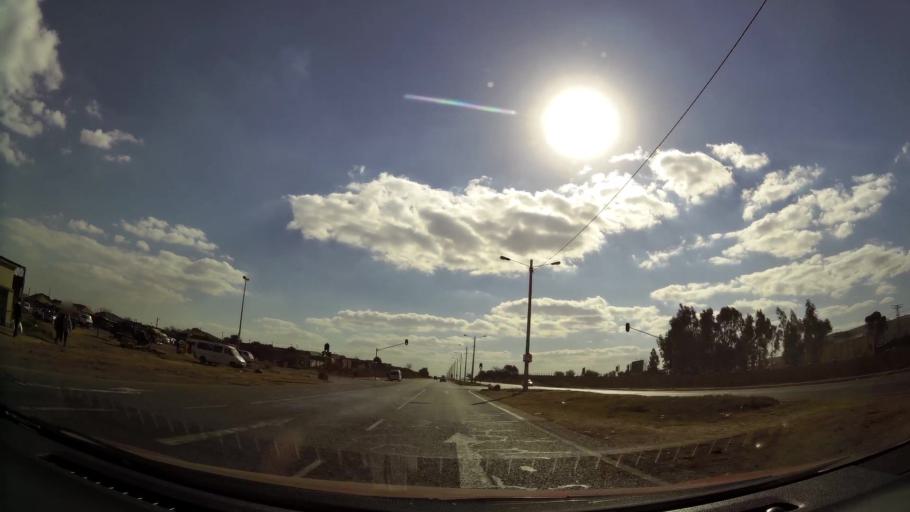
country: ZA
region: Gauteng
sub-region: Ekurhuleni Metropolitan Municipality
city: Tembisa
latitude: -25.9728
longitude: 28.2257
